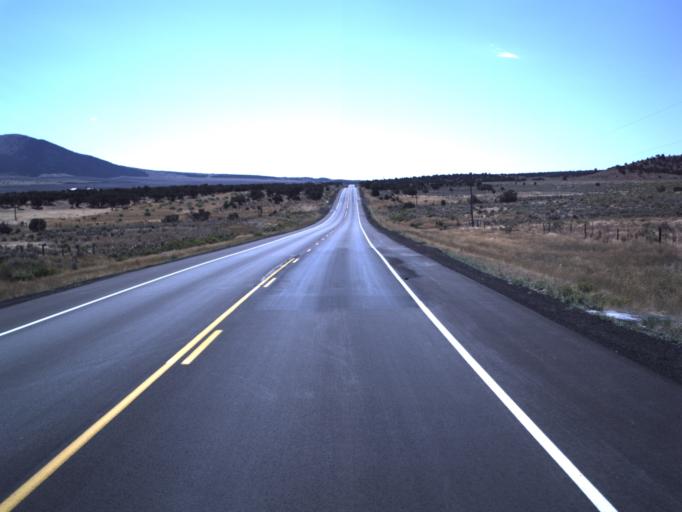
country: US
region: Utah
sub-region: Utah County
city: Eagle Mountain
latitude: 40.0493
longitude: -112.2953
